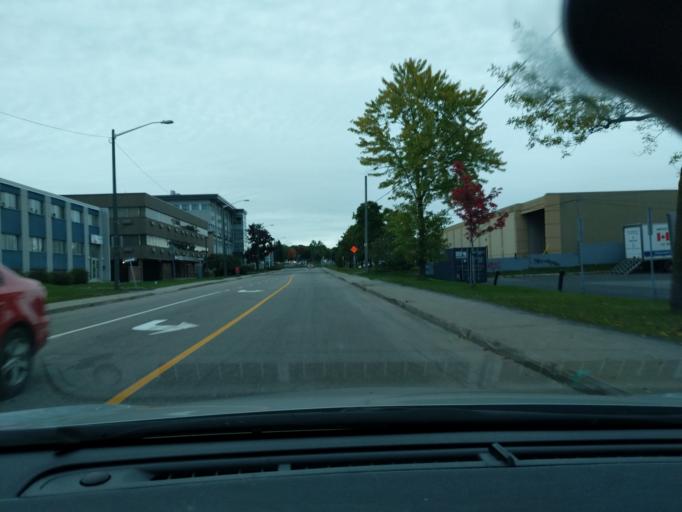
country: CA
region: Quebec
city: L'Ancienne-Lorette
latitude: 46.7643
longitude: -71.3168
